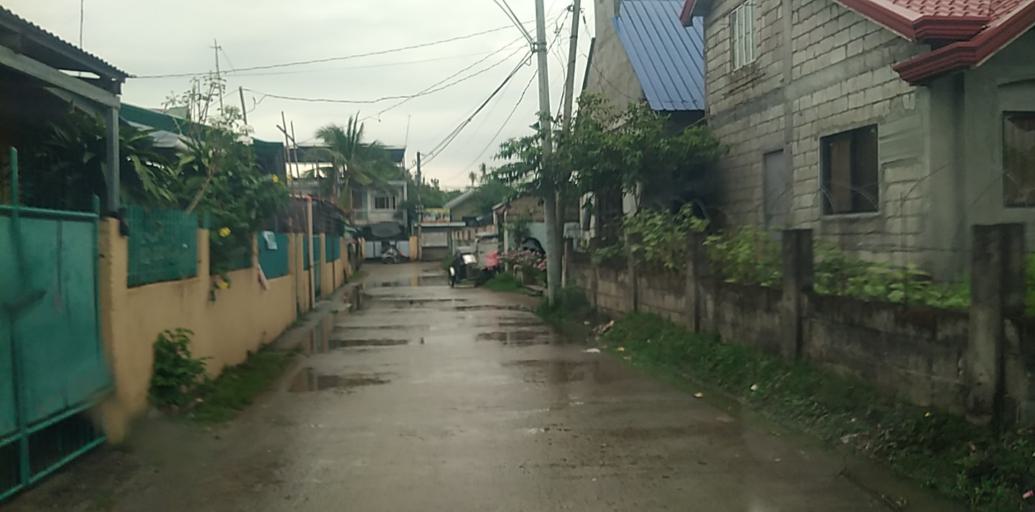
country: PH
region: Central Luzon
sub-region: Province of Pampanga
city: Anao
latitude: 15.1472
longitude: 120.7239
